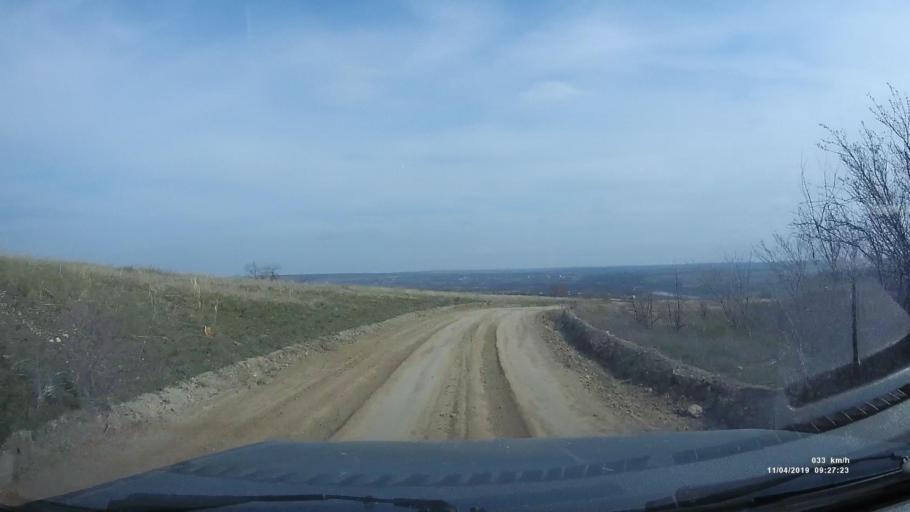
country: RU
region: Rostov
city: Staraya Stanitsa
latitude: 48.2662
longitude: 40.3668
